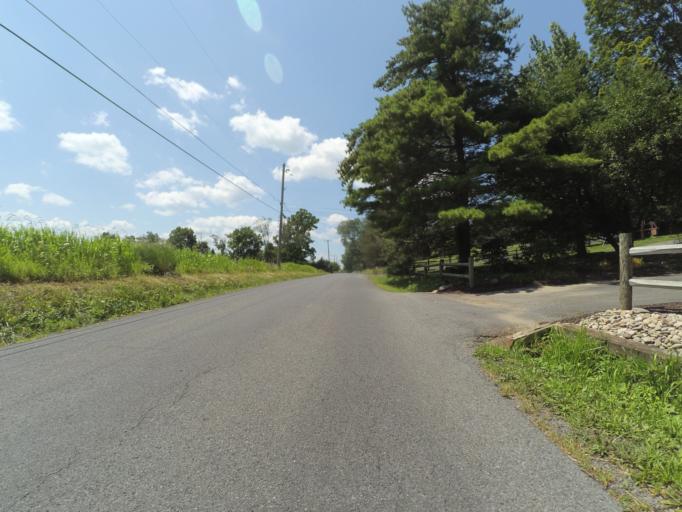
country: US
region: Pennsylvania
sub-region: Centre County
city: Boalsburg
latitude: 40.7984
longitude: -77.7925
